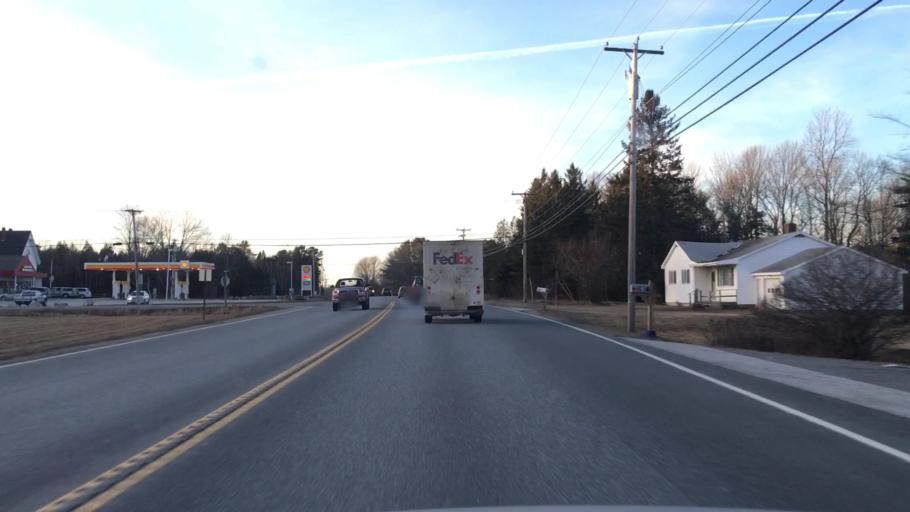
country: US
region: Maine
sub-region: Penobscot County
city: Holden
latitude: 44.7492
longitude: -68.6482
